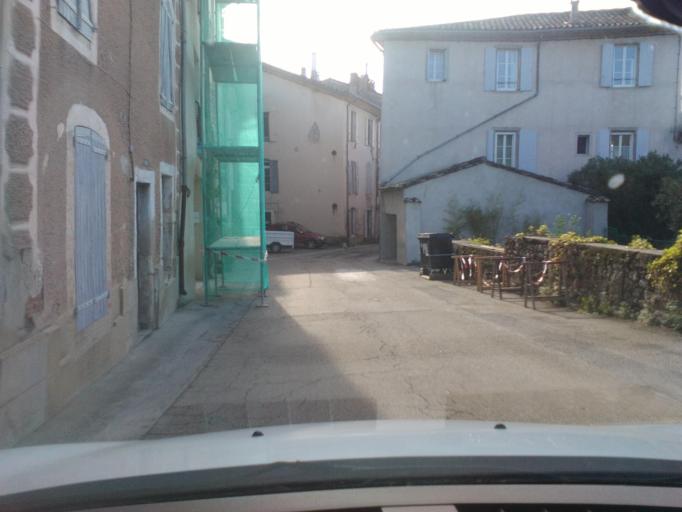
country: FR
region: Languedoc-Roussillon
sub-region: Departement du Gard
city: Lasalle
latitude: 44.0478
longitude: 3.8483
